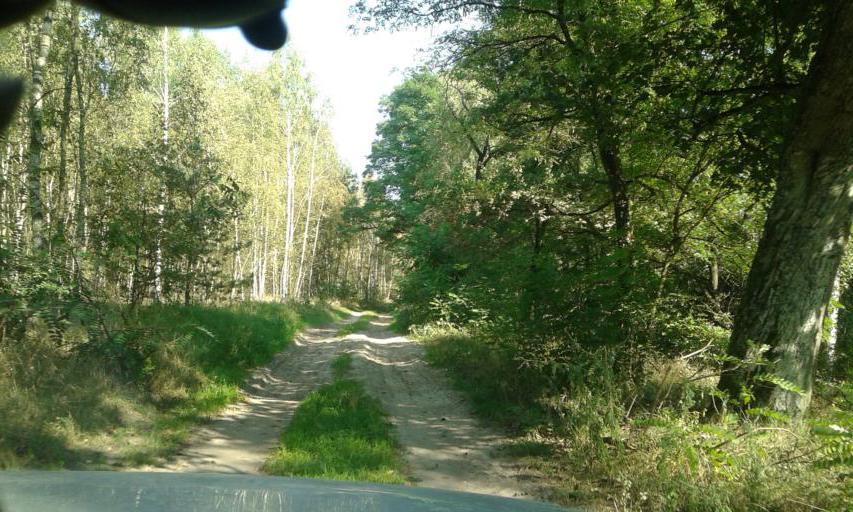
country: PL
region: West Pomeranian Voivodeship
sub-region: Powiat choszczenski
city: Choszczno
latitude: 53.1016
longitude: 15.4191
